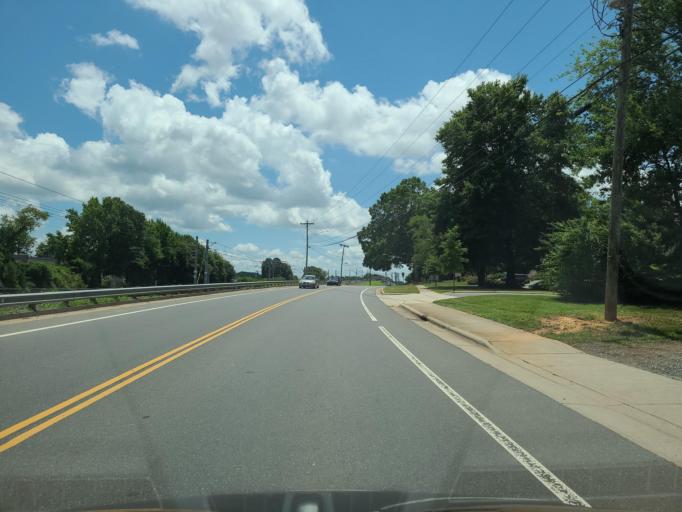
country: US
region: North Carolina
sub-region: Mecklenburg County
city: Pineville
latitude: 35.1568
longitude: -80.8772
